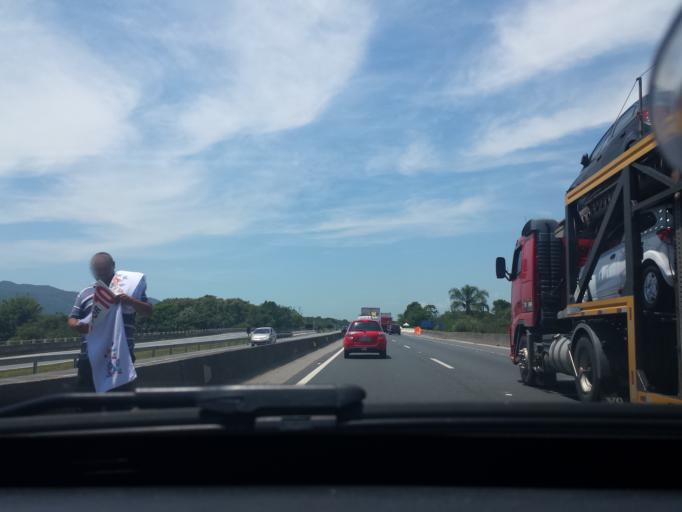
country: BR
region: Santa Catarina
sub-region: Itapema
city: Itapema
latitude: -27.1348
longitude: -48.6100
